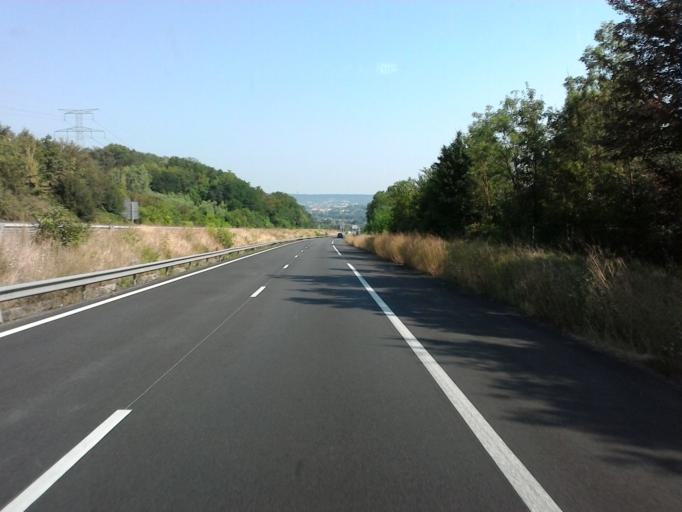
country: FR
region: Lorraine
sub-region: Departement de Meurthe-et-Moselle
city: Flavigny-sur-Moselle
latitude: 48.5695
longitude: 6.1760
